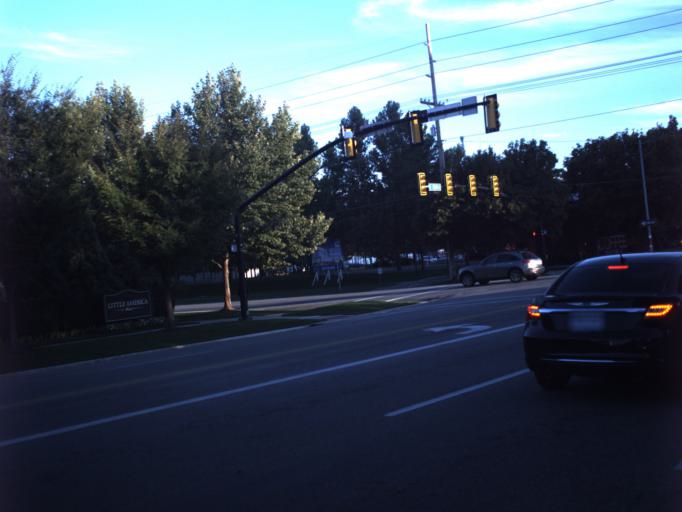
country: US
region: Utah
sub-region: Salt Lake County
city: Salt Lake City
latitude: 40.7567
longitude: -111.8941
